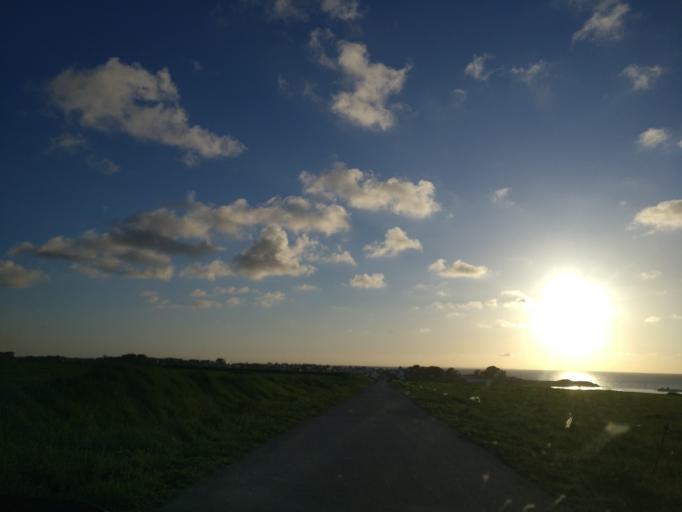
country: FR
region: Brittany
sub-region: Departement du Finistere
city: Lampaul-Plouarzel
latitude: 48.4674
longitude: -4.7464
